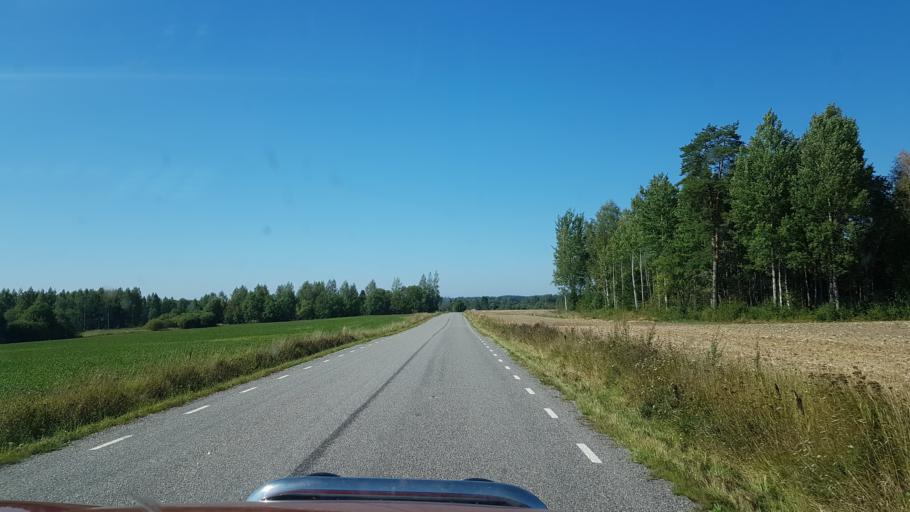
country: EE
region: Polvamaa
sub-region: Polva linn
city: Polva
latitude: 58.2095
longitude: 27.1264
